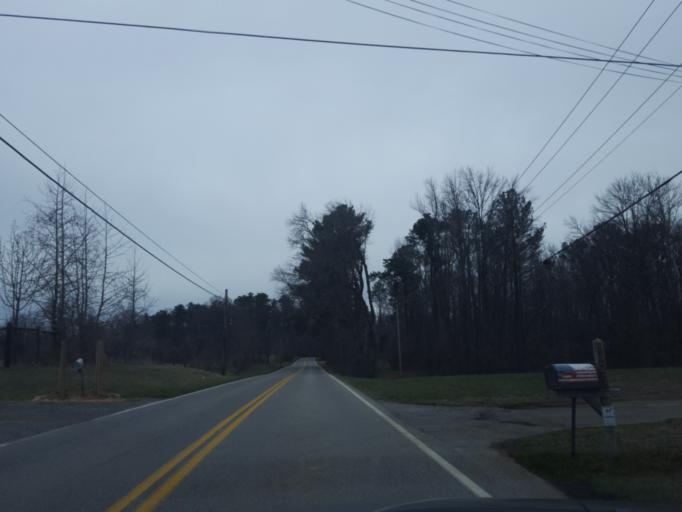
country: US
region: Maryland
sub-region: Calvert County
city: Lusby
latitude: 38.4120
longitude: -76.5029
